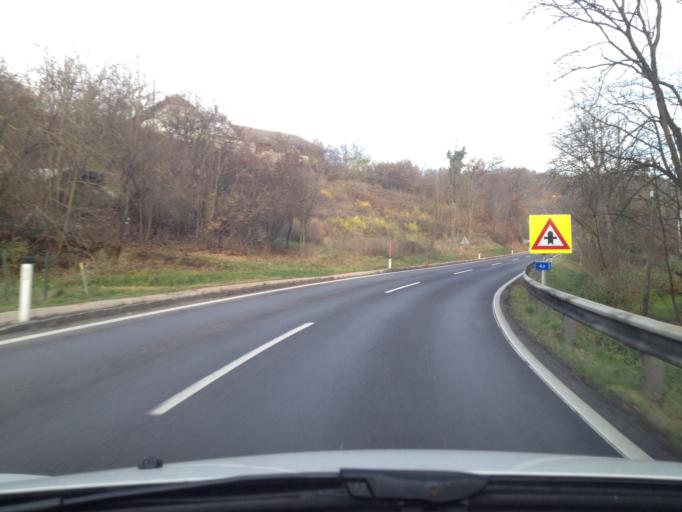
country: AT
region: Upper Austria
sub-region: Politischer Bezirk Urfahr-Umgebung
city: Altenberg bei Linz
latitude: 48.3349
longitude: 14.3332
